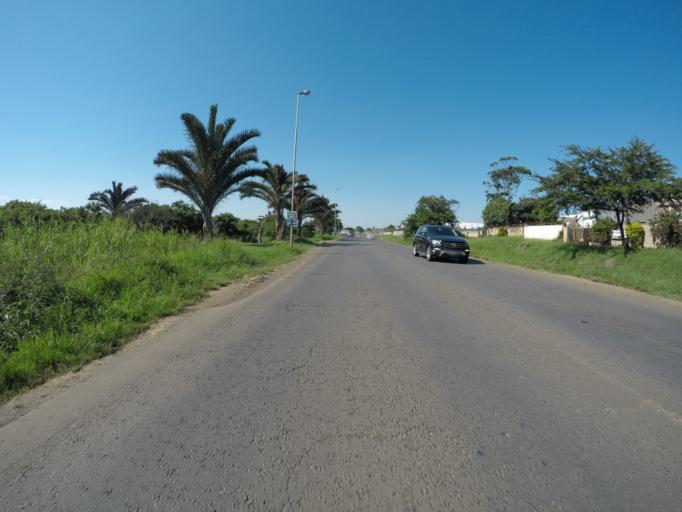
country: ZA
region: KwaZulu-Natal
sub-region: uThungulu District Municipality
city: Empangeni
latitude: -28.7661
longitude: 31.9057
